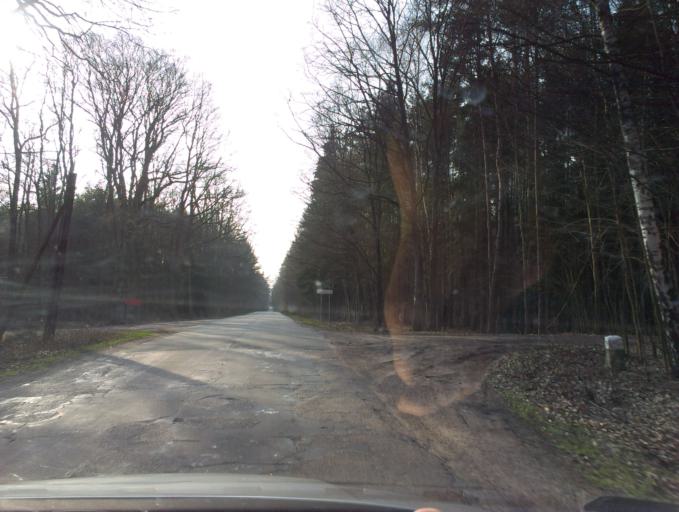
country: PL
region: Kujawsko-Pomorskie
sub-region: Powiat sepolenski
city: Sypniewo
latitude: 53.4506
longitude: 17.3831
